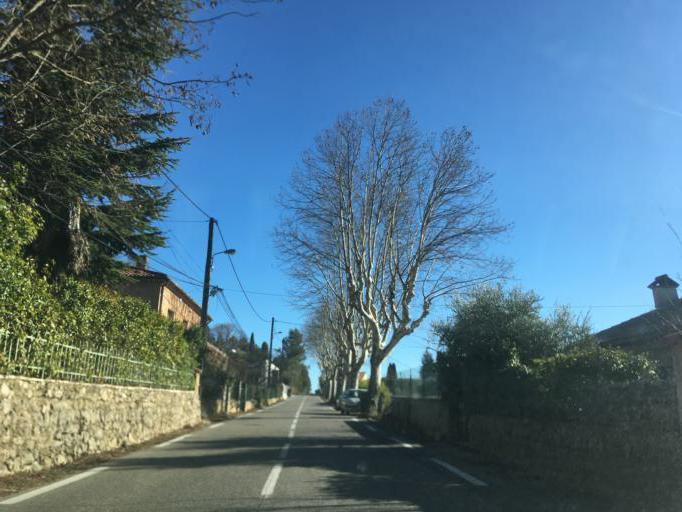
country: FR
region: Provence-Alpes-Cote d'Azur
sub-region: Departement du Var
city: Barjols
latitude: 43.5966
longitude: 5.9626
